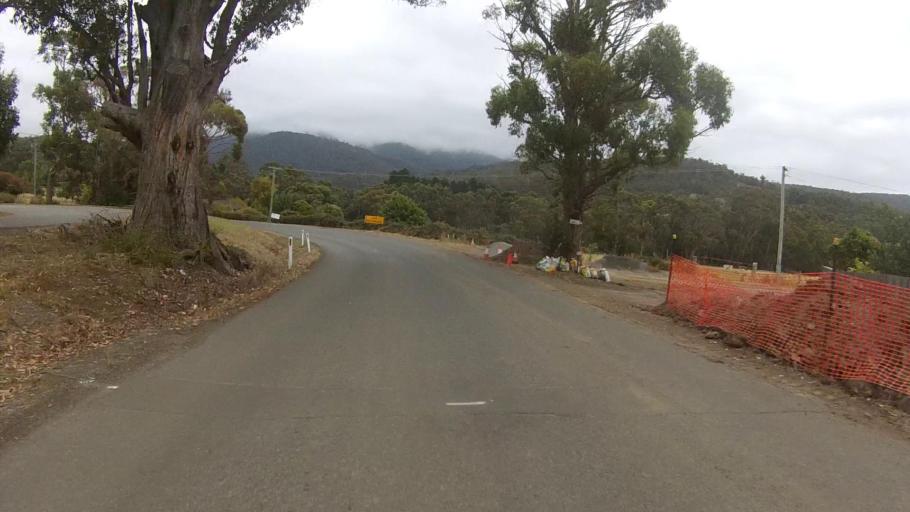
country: AU
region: Tasmania
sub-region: Kingborough
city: Kingston
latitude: -42.9660
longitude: 147.2868
